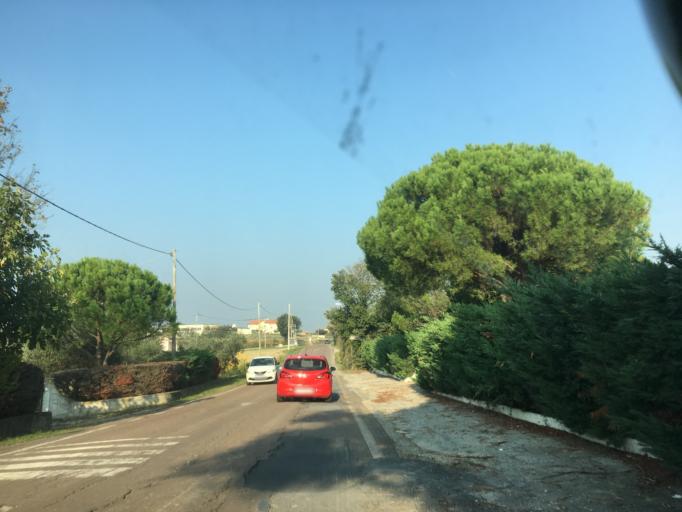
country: IT
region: Emilia-Romagna
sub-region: Provincia di Rimini
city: San Clemente
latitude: 43.9464
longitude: 12.6180
